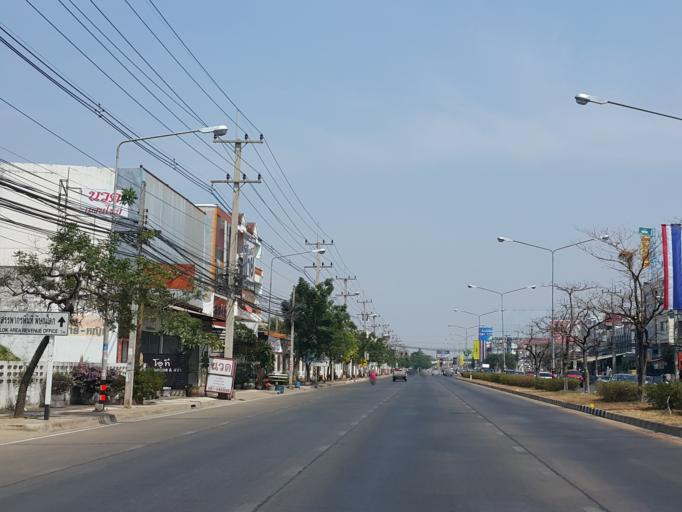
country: TH
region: Phitsanulok
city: Phitsanulok
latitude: 16.8280
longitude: 100.2534
